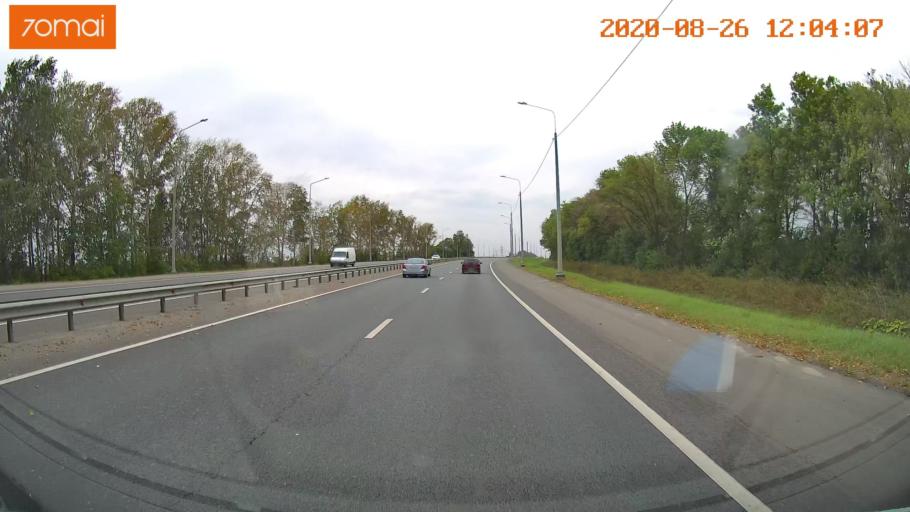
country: RU
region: Rjazan
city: Kiritsy
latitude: 54.3066
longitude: 40.1943
